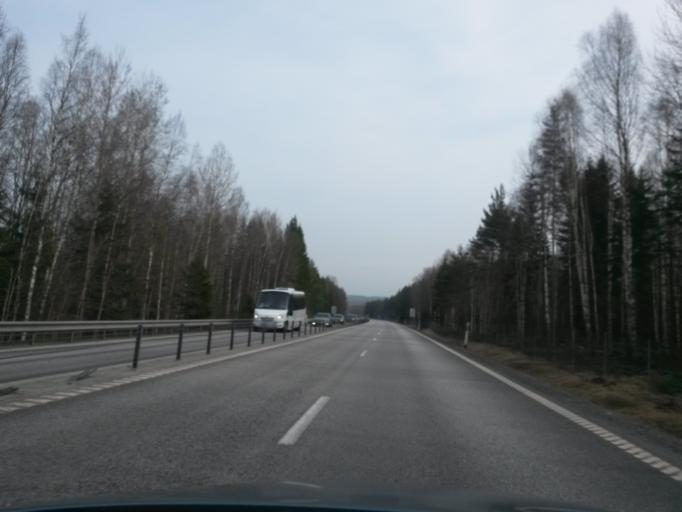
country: SE
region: Vaestra Goetaland
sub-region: Gullspangs Kommun
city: Anderstorp
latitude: 58.9228
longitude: 14.4071
